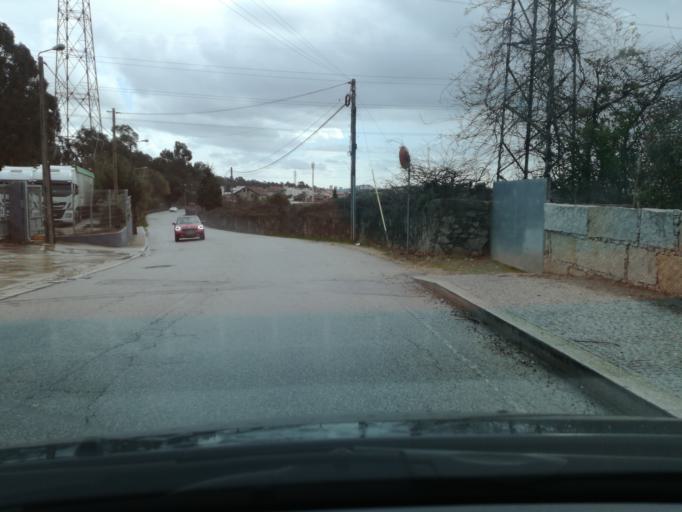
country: PT
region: Porto
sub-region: Valongo
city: Ermesinde
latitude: 41.2359
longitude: -8.5444
